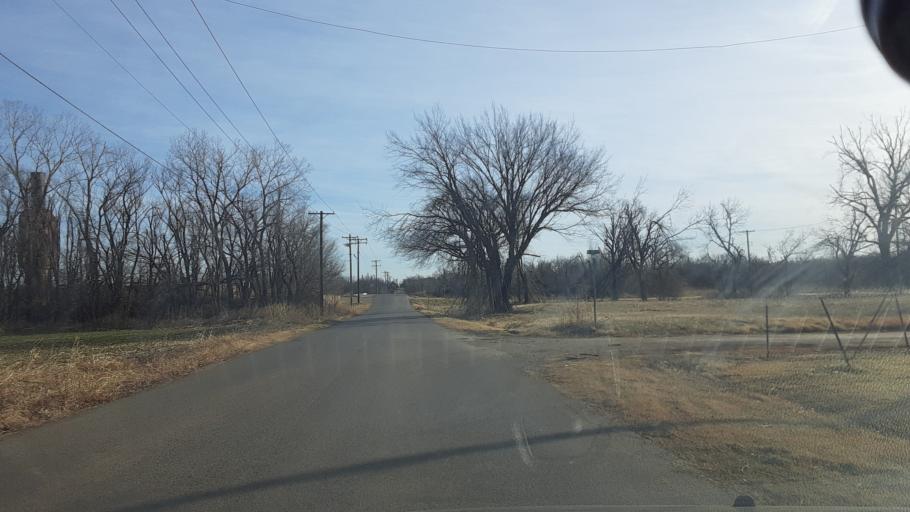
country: US
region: Oklahoma
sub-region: Logan County
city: Guthrie
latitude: 35.8853
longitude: -97.4317
